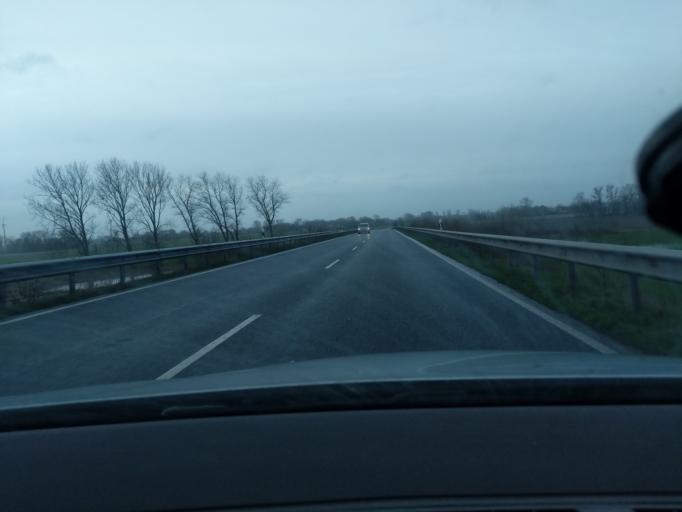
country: DE
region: Lower Saxony
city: Otterndorf
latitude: 53.8019
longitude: 8.9199
